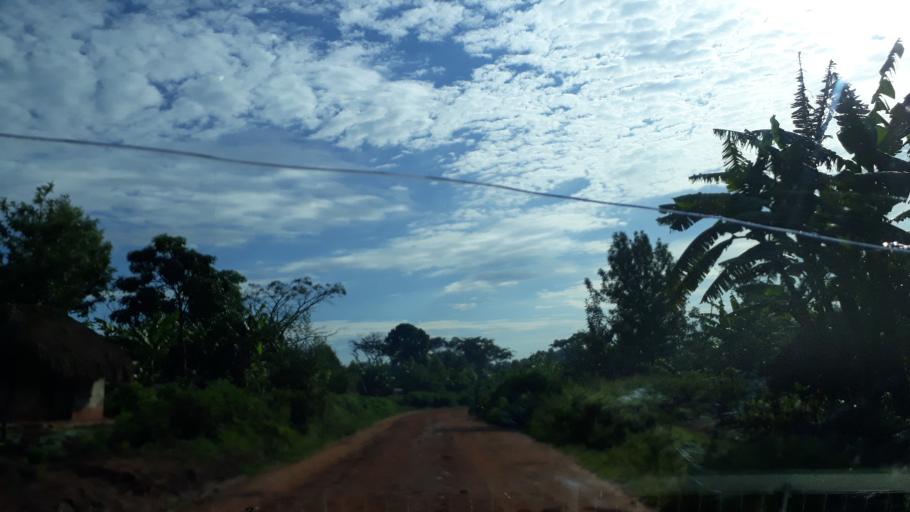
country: UG
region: Northern Region
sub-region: Zombo District
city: Paidha
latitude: 2.2523
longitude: 30.9069
